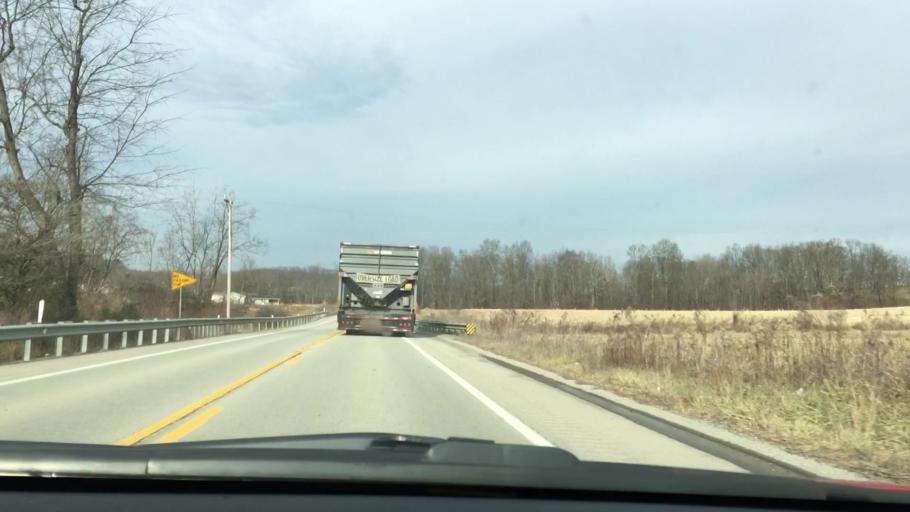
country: US
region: Pennsylvania
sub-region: Greene County
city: Fairdale
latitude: 39.8680
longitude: -79.9735
